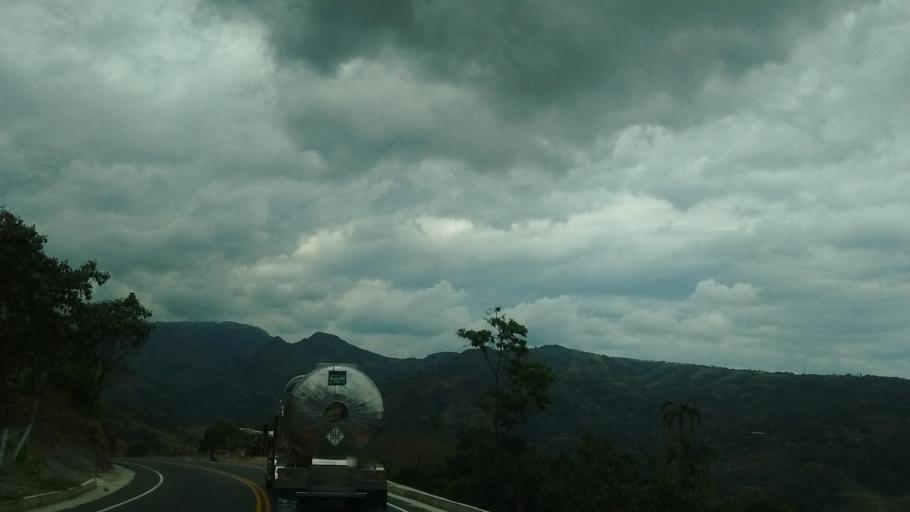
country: CO
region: Cauca
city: Rosas
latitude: 2.2905
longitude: -76.7084
